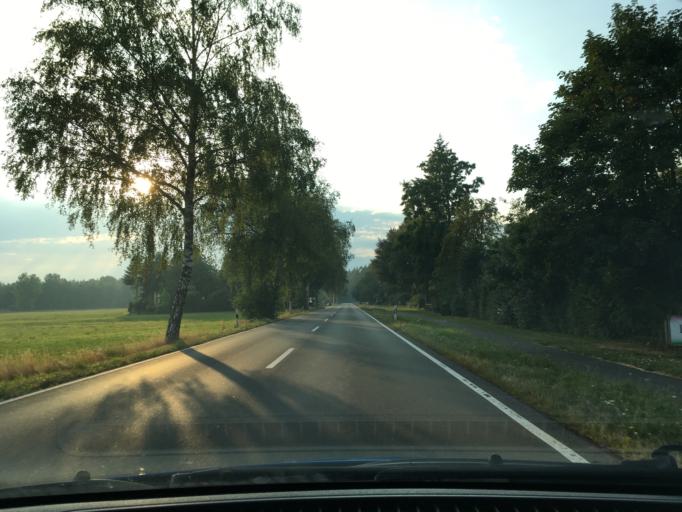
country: DE
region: Lower Saxony
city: Hermannsburg
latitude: 52.7359
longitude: 10.0814
